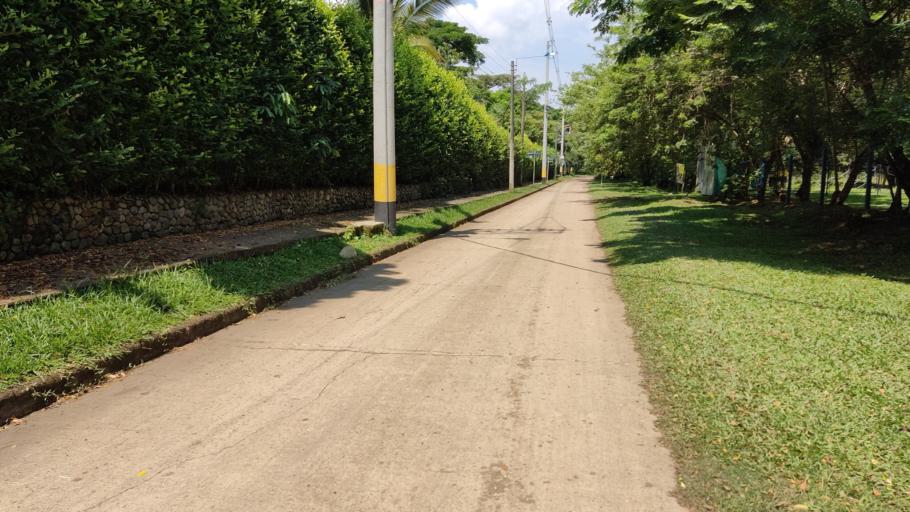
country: CO
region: Valle del Cauca
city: Jamundi
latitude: 3.3169
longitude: -76.5429
